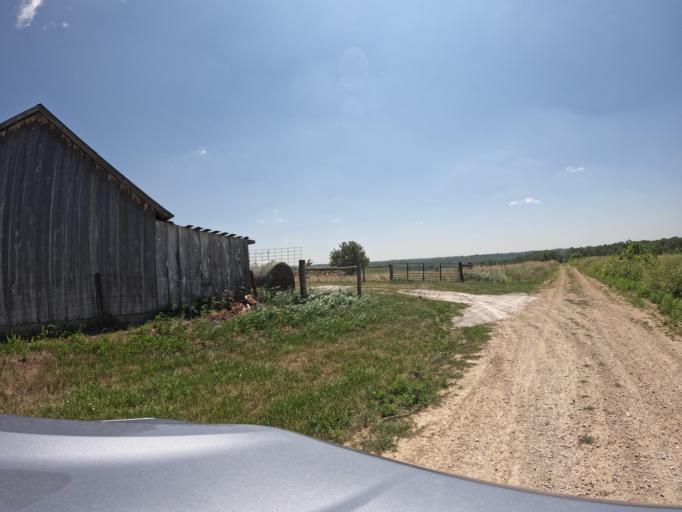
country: US
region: Iowa
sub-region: Keokuk County
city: Sigourney
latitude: 41.2567
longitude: -92.1806
